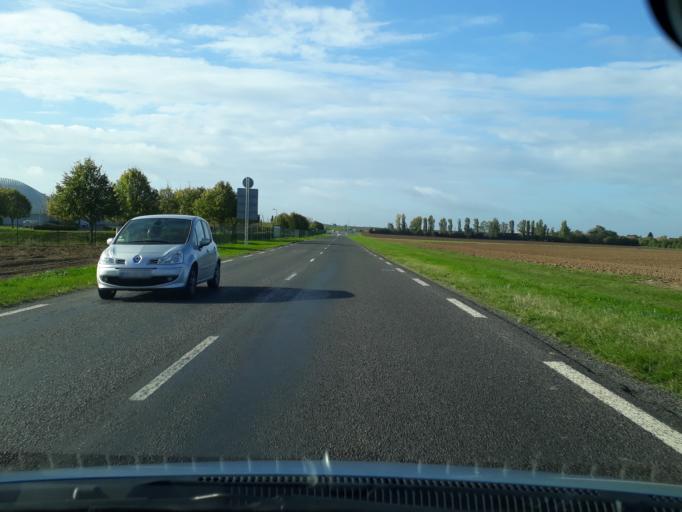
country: FR
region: Centre
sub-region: Departement du Loiret
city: Malesherbes
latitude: 48.2445
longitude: 2.3364
